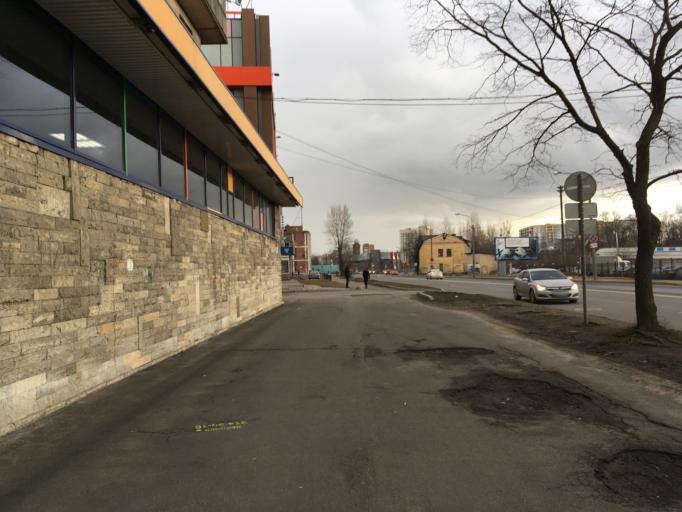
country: RU
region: St.-Petersburg
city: Centralniy
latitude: 59.9401
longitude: 30.4144
